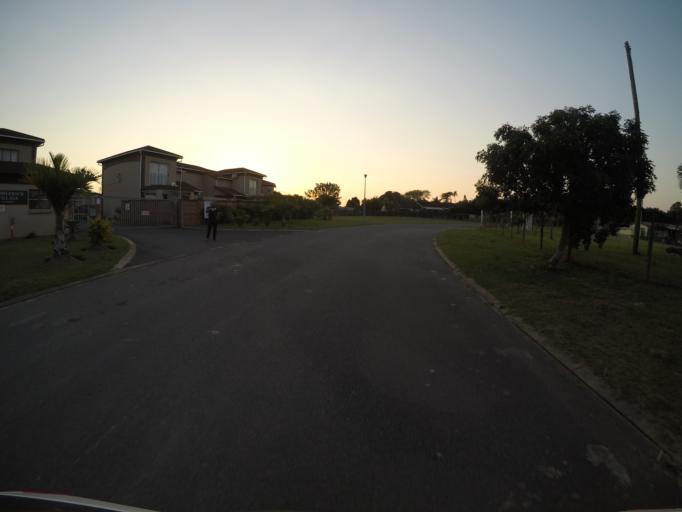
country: ZA
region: KwaZulu-Natal
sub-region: uThungulu District Municipality
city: Richards Bay
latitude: -28.7706
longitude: 32.1215
